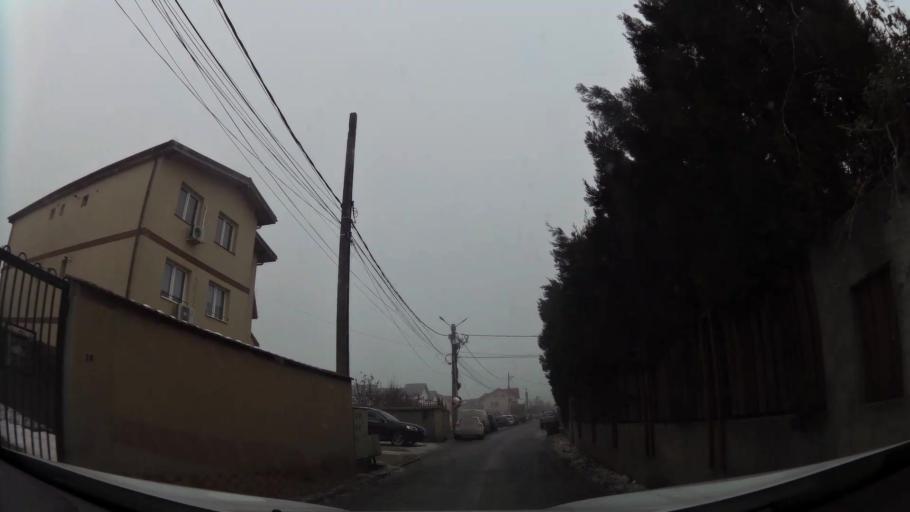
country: RO
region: Ilfov
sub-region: Comuna Chiajna
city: Rosu
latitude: 44.4456
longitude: 26.0081
